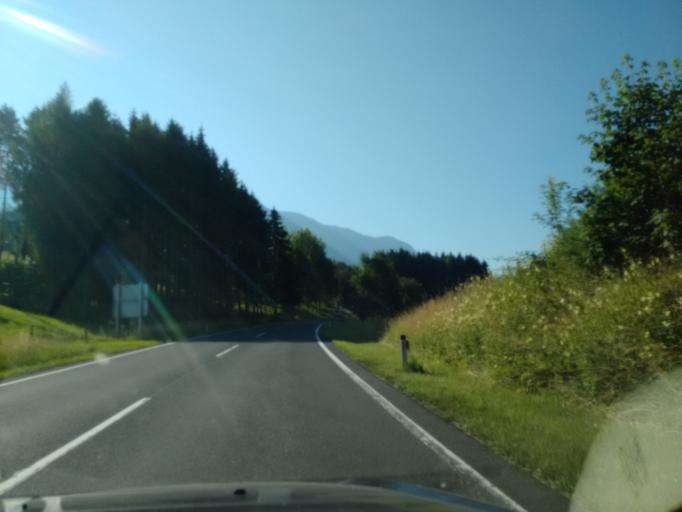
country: AT
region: Upper Austria
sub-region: Politischer Bezirk Gmunden
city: Bad Goisern
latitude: 47.6198
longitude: 13.6515
